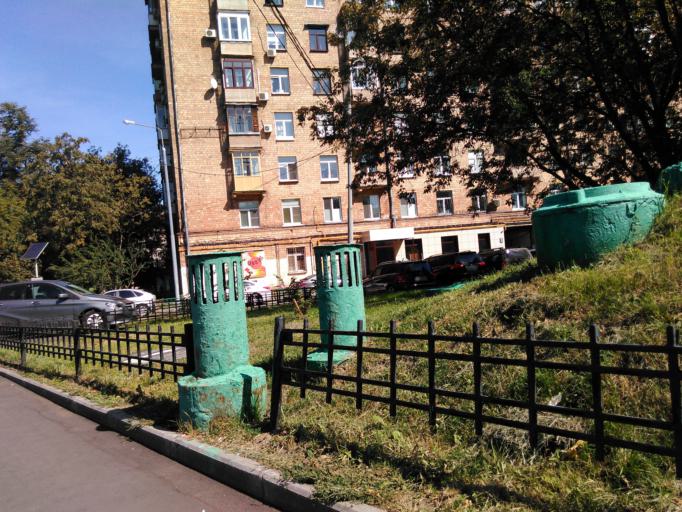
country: RU
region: Moscow
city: Novyye Cheremushki
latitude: 55.7012
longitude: 37.5795
